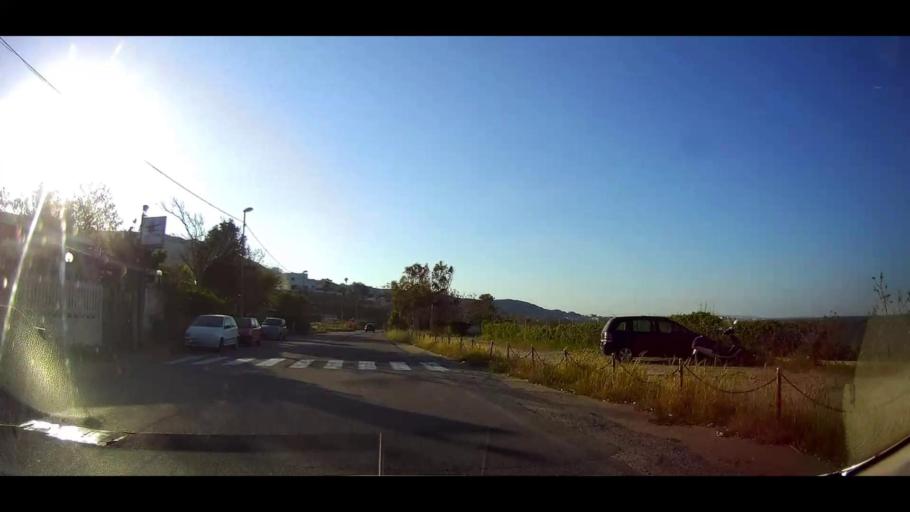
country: IT
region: Calabria
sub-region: Provincia di Crotone
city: Crotone
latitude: 39.0505
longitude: 17.1417
